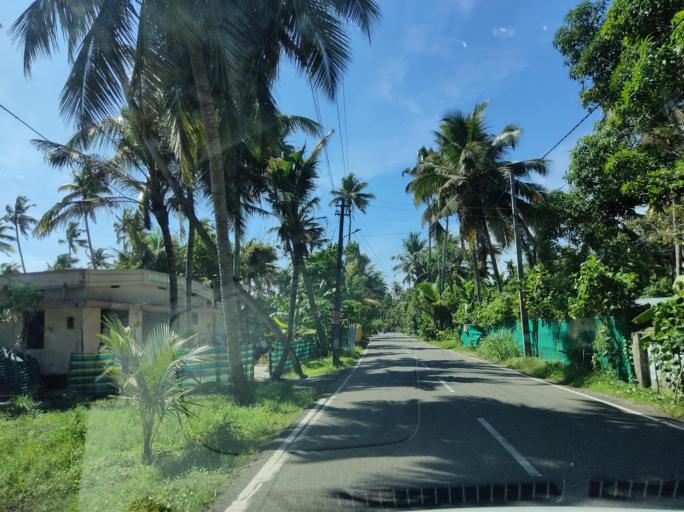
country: IN
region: Kerala
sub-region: Alappuzha
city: Kayankulam
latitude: 9.1863
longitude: 76.4410
